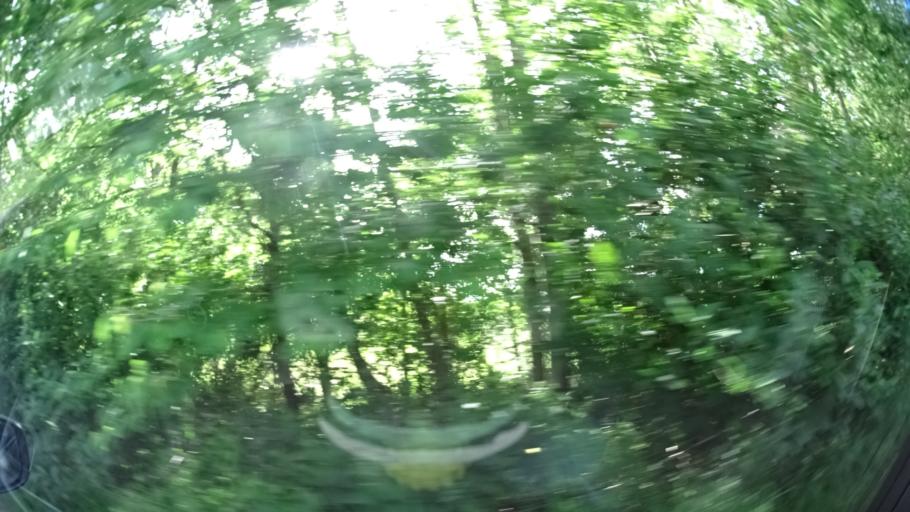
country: DK
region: Central Jutland
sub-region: Norddjurs Kommune
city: Grenaa
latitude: 56.4706
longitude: 10.7157
